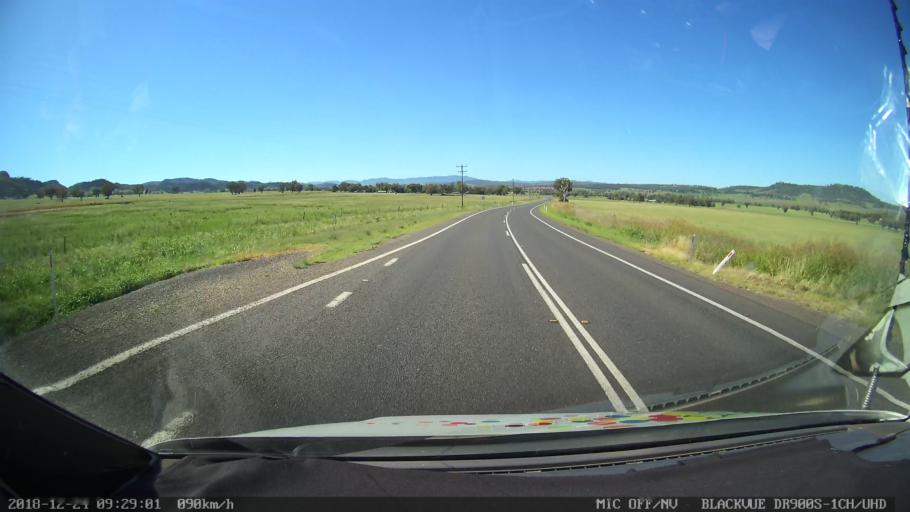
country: AU
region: New South Wales
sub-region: Liverpool Plains
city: Quirindi
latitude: -31.5447
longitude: 150.6926
